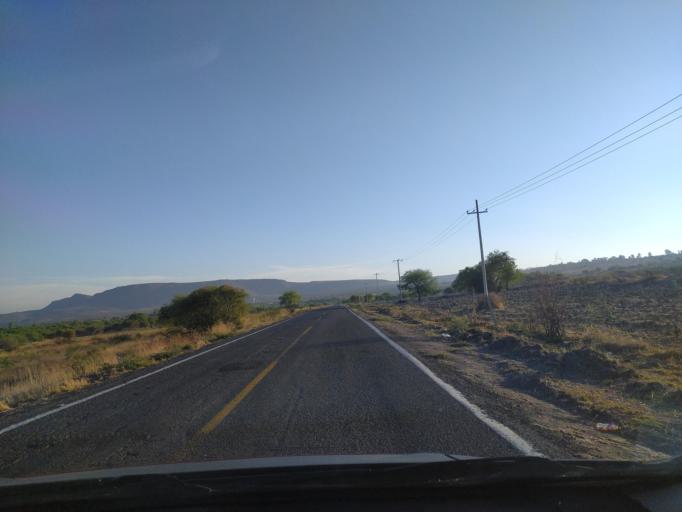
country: MX
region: Guanajuato
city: Ciudad Manuel Doblado
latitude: 20.7358
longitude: -101.8276
